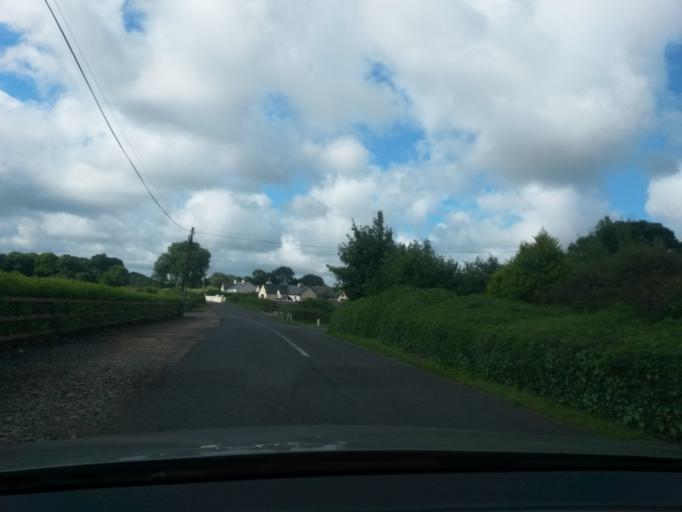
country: IE
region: Connaught
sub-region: Sligo
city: Sligo
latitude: 54.2514
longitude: -8.4977
